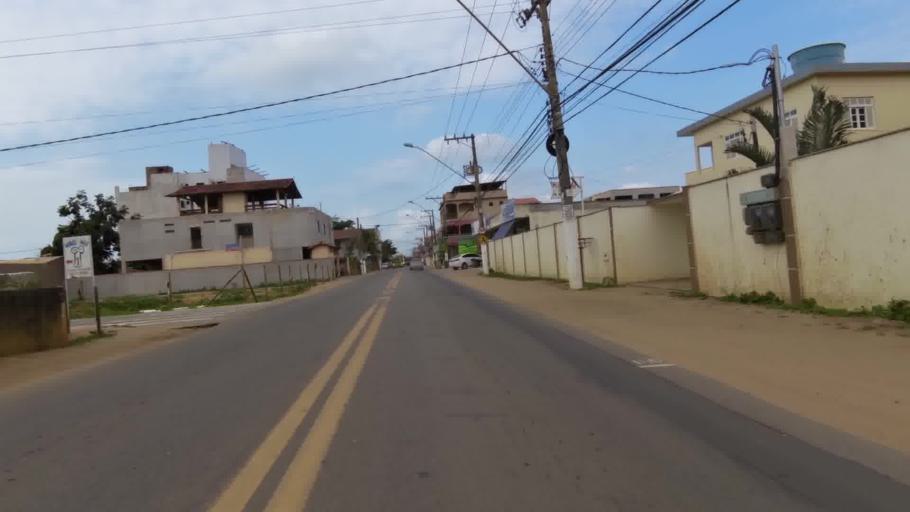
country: BR
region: Espirito Santo
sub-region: Piuma
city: Piuma
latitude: -20.8977
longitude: -40.7773
